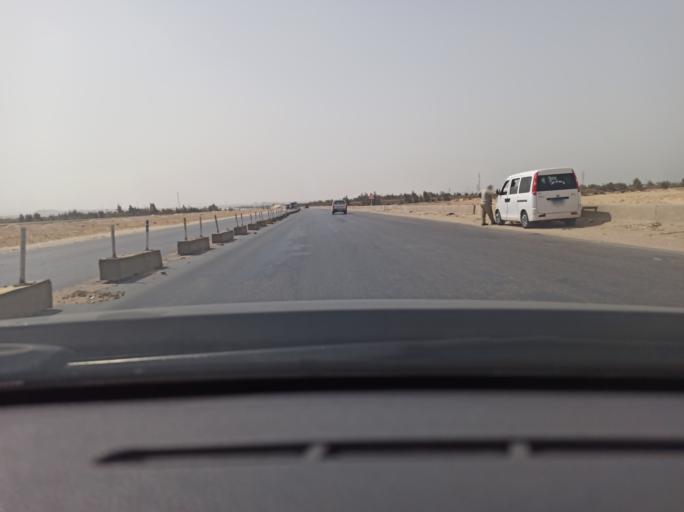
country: EG
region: Muhafazat al Fayyum
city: Al Wasitah
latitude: 29.2783
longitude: 31.2670
